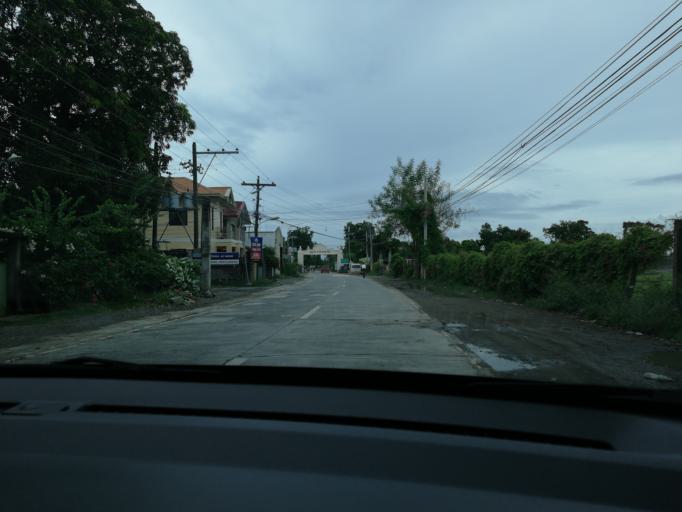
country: PH
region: Ilocos
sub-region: Province of Ilocos Sur
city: Bantay
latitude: 17.5838
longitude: 120.3838
